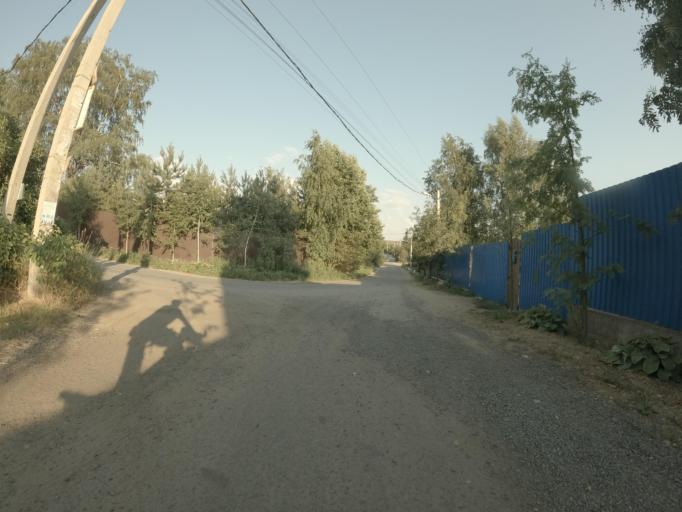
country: RU
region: Leningrad
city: Koltushi
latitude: 59.8968
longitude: 30.6855
